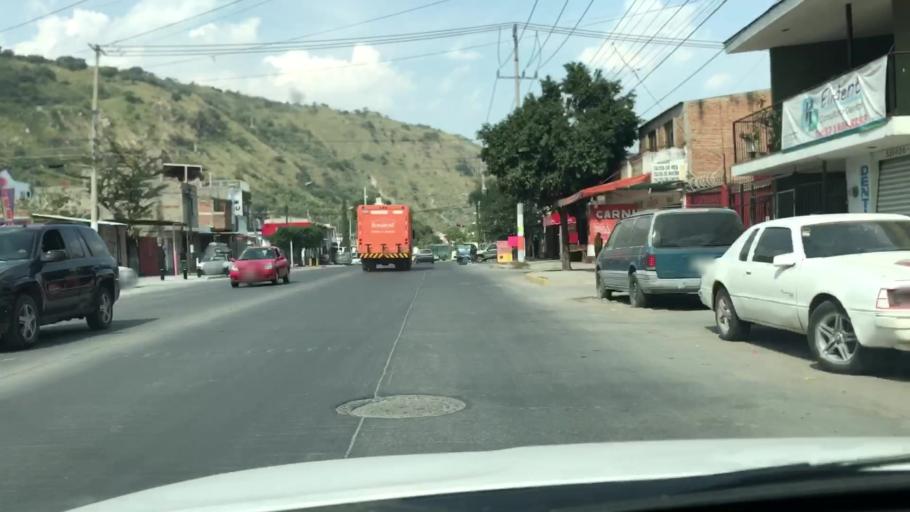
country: MX
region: Jalisco
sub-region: Tlajomulco de Zuniga
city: Palomar
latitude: 20.6447
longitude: -103.4603
